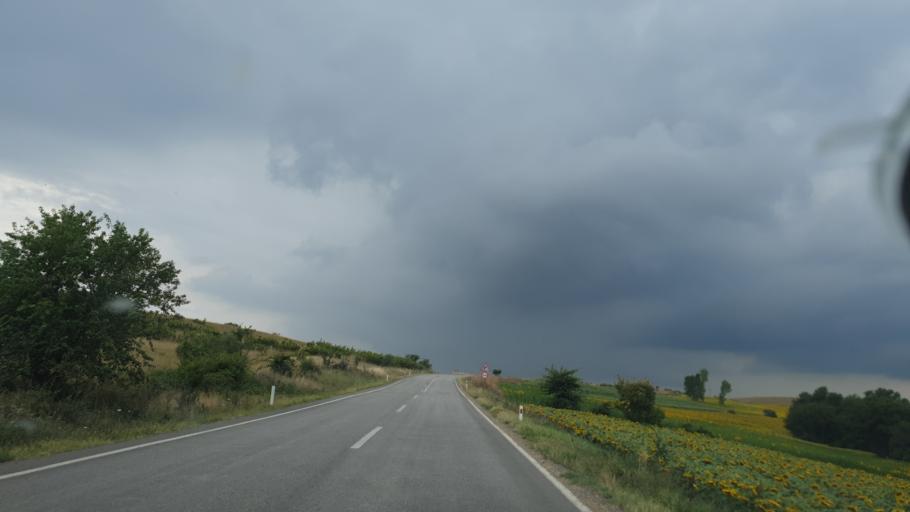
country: TR
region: Tekirdag
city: Hayrabolu
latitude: 41.2252
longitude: 27.0285
